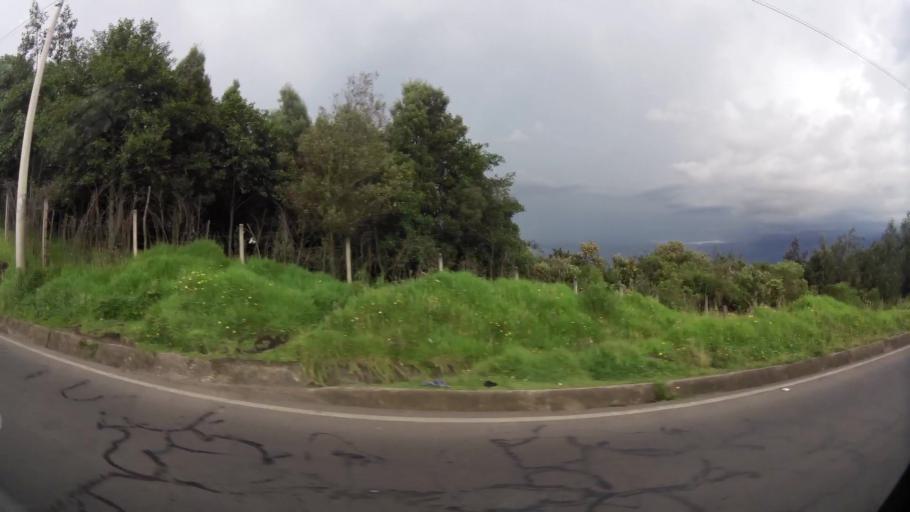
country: EC
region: Pichincha
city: Sangolqui
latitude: -0.3120
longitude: -78.5222
